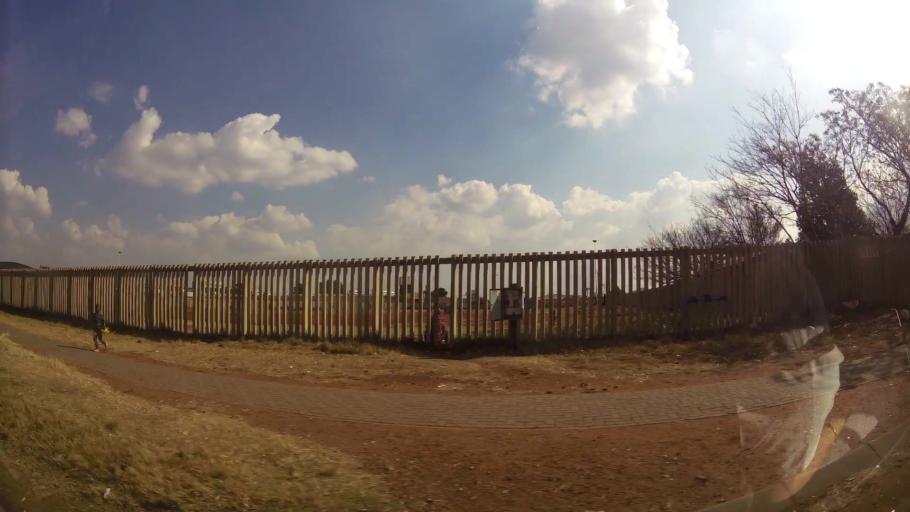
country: ZA
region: Gauteng
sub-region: Ekurhuleni Metropolitan Municipality
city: Germiston
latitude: -26.3291
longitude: 28.1556
